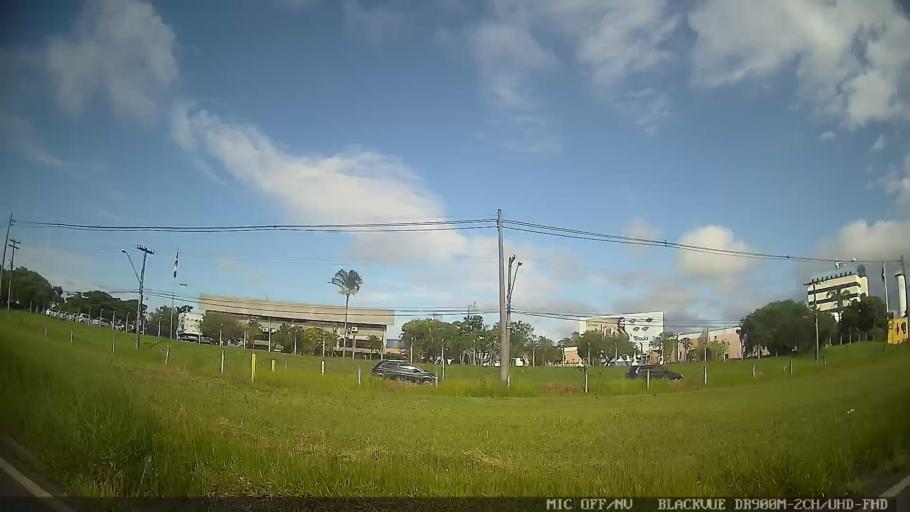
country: BR
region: Sao Paulo
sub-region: Jarinu
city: Jarinu
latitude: -23.0468
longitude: -46.6743
